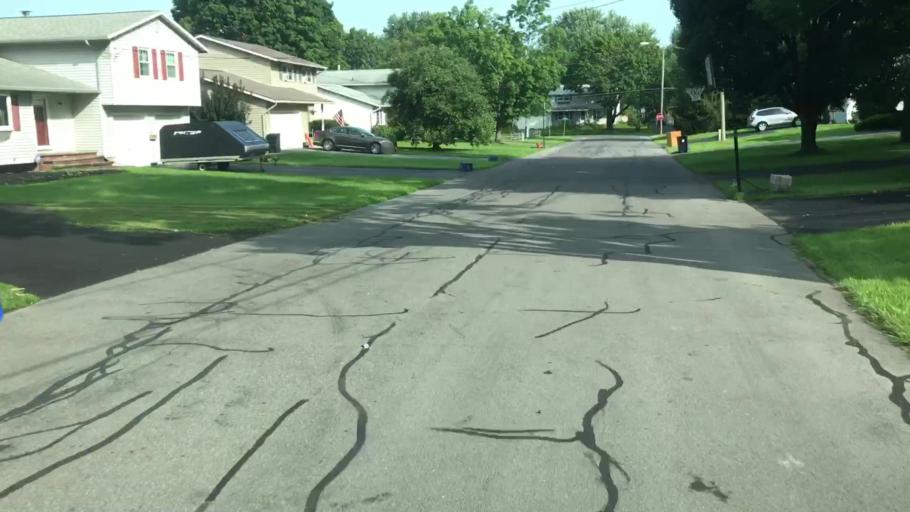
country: US
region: New York
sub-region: Onondaga County
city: Liverpool
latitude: 43.1334
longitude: -76.2180
